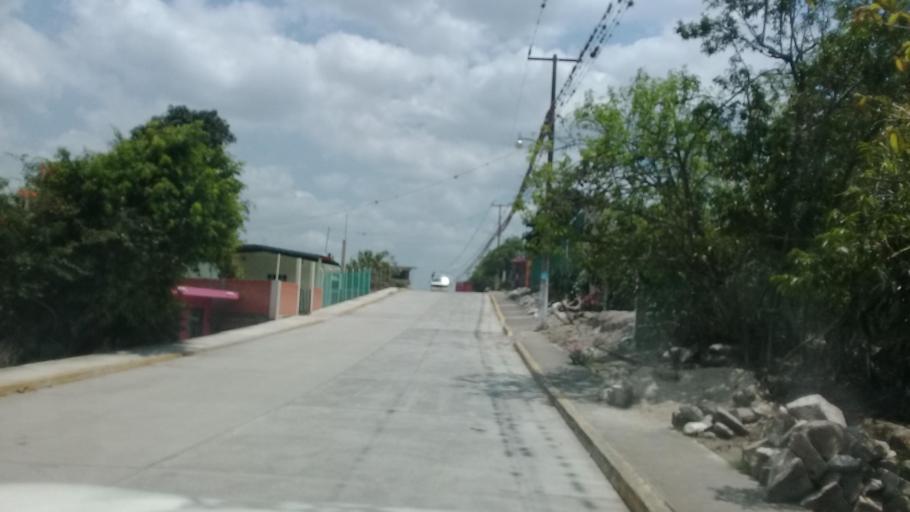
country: MX
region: Veracruz
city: Jalcomulco
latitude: 19.3954
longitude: -96.7889
